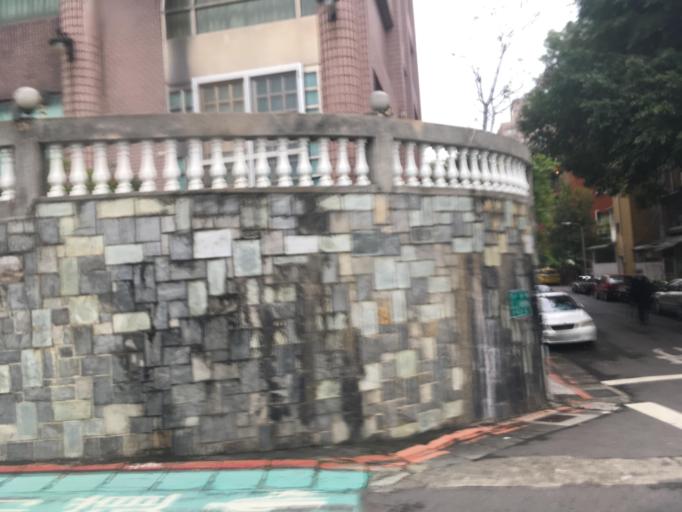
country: TW
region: Taipei
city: Taipei
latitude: 25.1303
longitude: 121.5282
